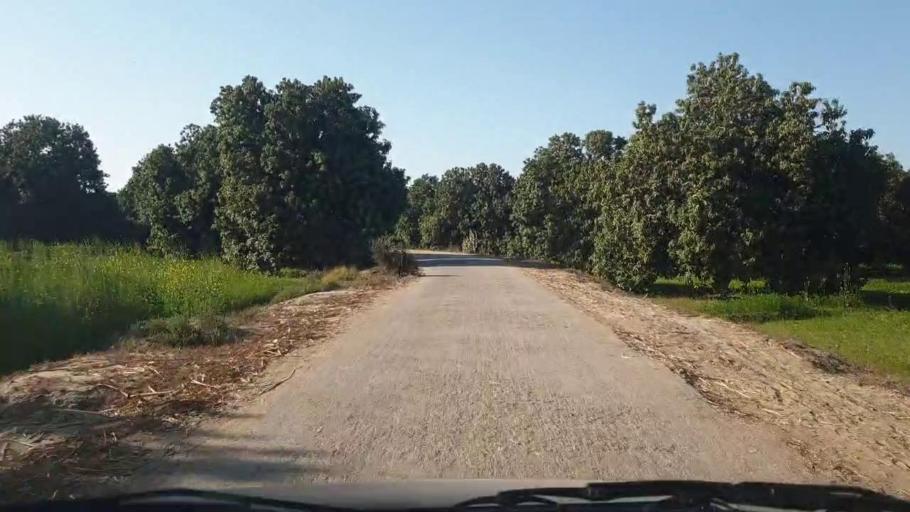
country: PK
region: Sindh
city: Samaro
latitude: 25.3564
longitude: 69.3040
